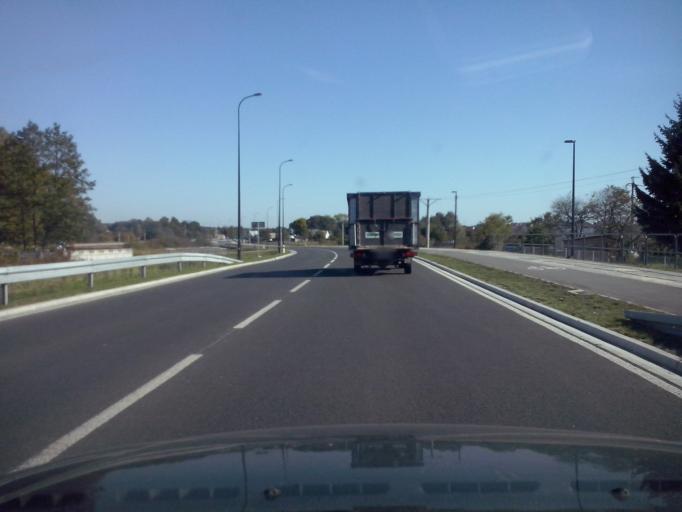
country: PL
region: Lublin Voivodeship
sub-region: Powiat bilgorajski
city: Bilgoraj
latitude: 50.5487
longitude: 22.7163
